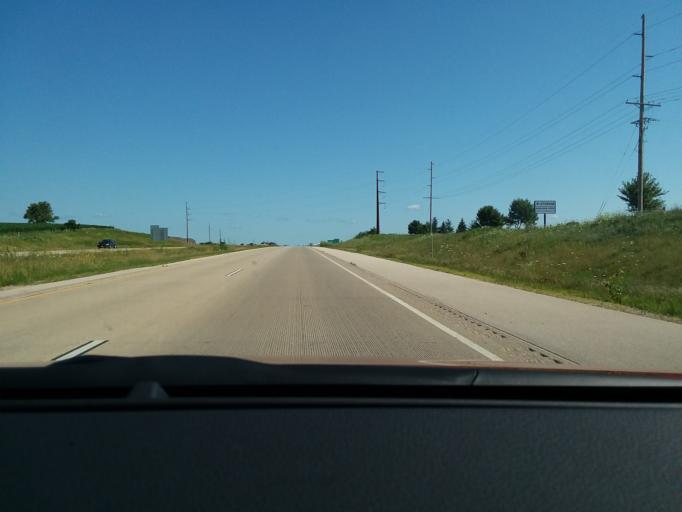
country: US
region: Wisconsin
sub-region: Dane County
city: Windsor
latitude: 43.2072
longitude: -89.3229
